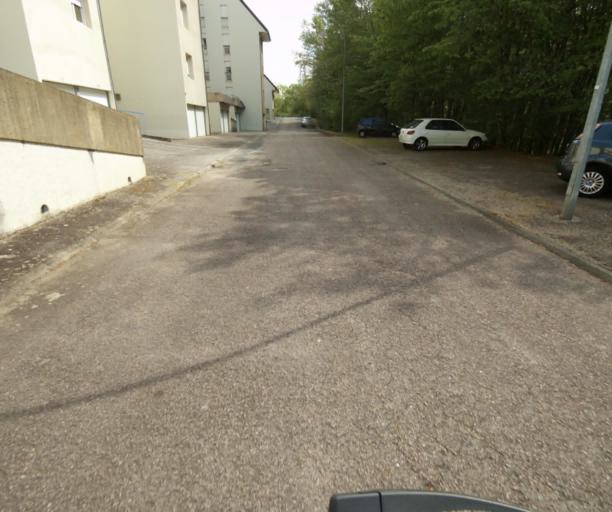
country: FR
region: Limousin
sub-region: Departement de la Correze
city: Tulle
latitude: 45.2768
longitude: 1.7659
